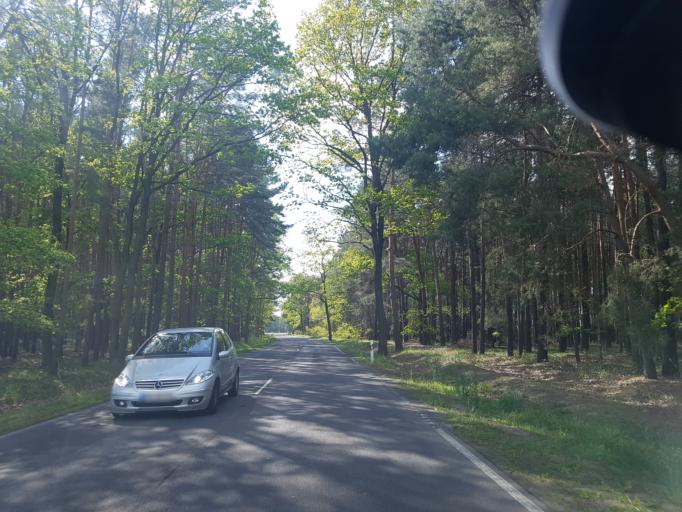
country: DE
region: Brandenburg
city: Spremberg
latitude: 51.6751
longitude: 14.4331
